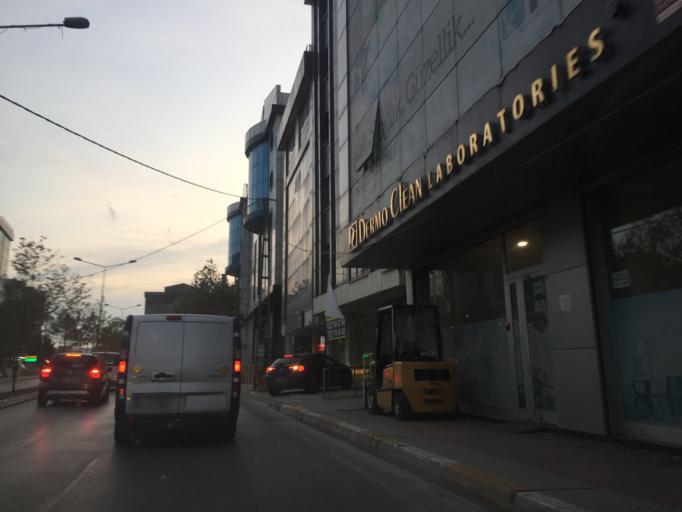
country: TR
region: Istanbul
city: Samandira
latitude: 40.9846
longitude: 29.2224
